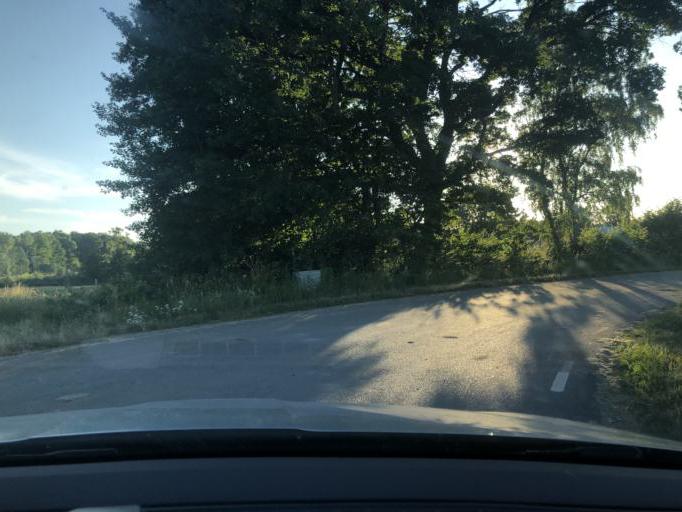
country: SE
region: Blekinge
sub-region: Karlshamns Kommun
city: Morrum
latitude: 56.1397
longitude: 14.6466
